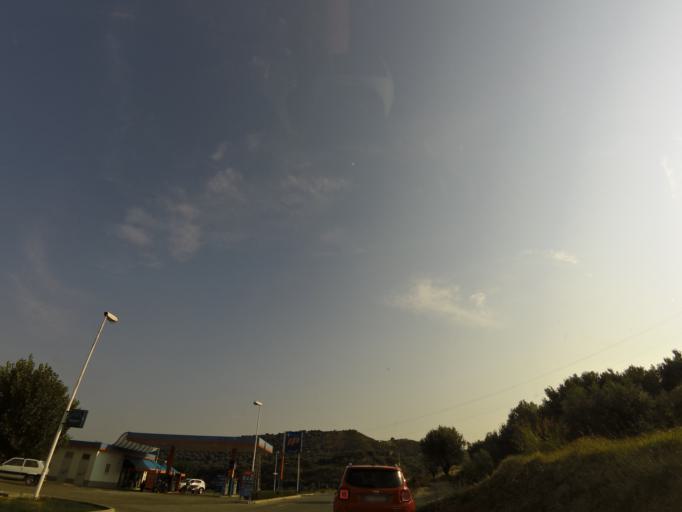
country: IT
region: Calabria
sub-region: Provincia di Reggio Calabria
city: Stilo
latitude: 38.4659
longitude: 16.5022
